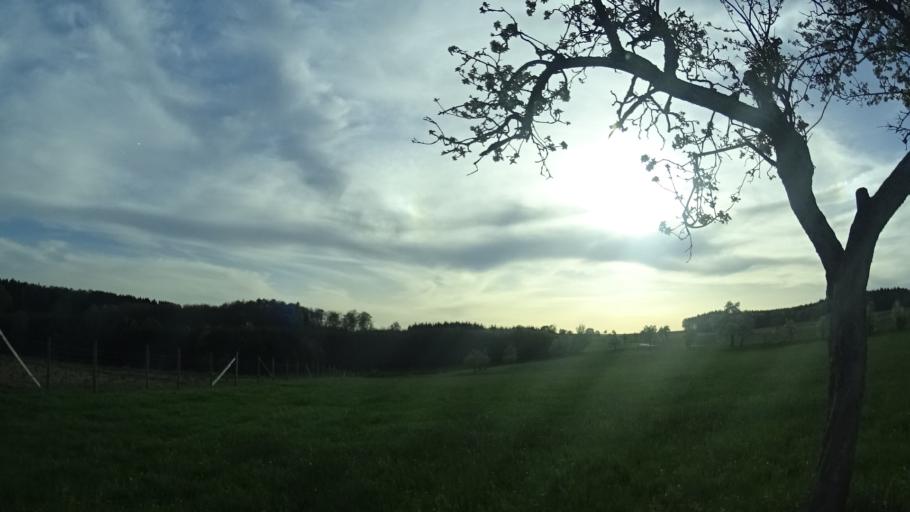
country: DE
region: Baden-Wuerttemberg
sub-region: Karlsruhe Region
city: Limbach
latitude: 49.4756
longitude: 9.1719
